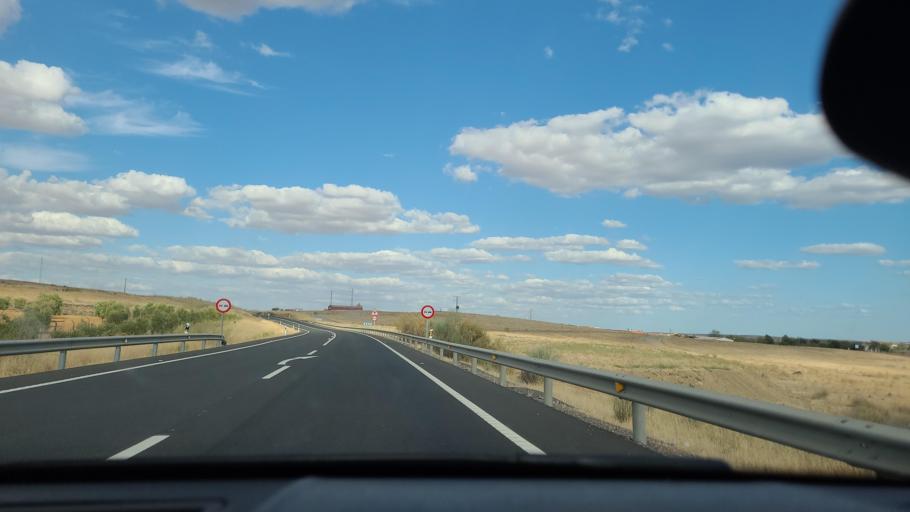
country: ES
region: Extremadura
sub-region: Provincia de Badajoz
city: Ahillones
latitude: 38.2596
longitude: -5.8742
